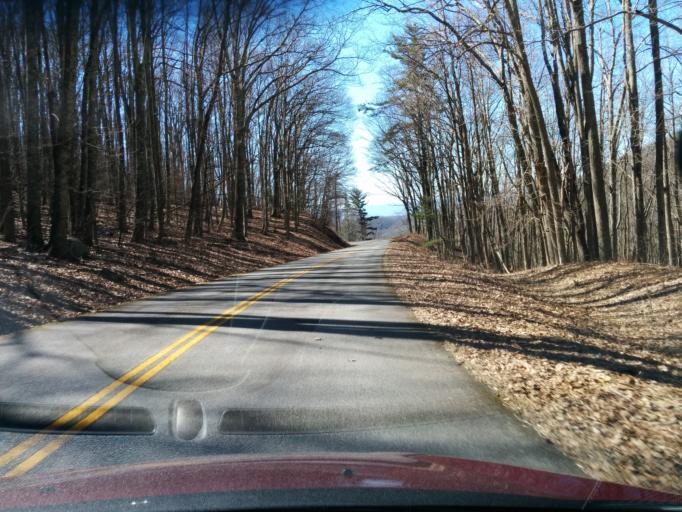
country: US
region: Virginia
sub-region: City of Buena Vista
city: Buena Vista
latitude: 37.8020
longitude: -79.1897
